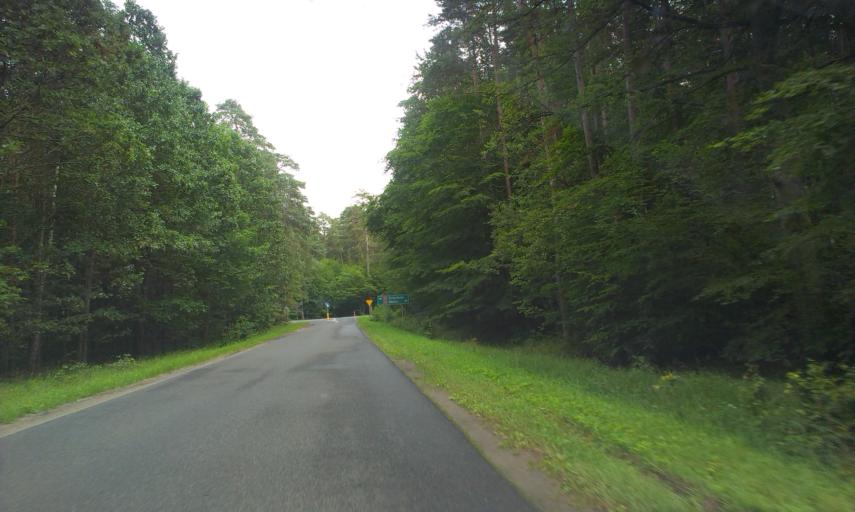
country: PL
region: Greater Poland Voivodeship
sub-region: Powiat zlotowski
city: Okonek
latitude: 53.5319
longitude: 16.9403
